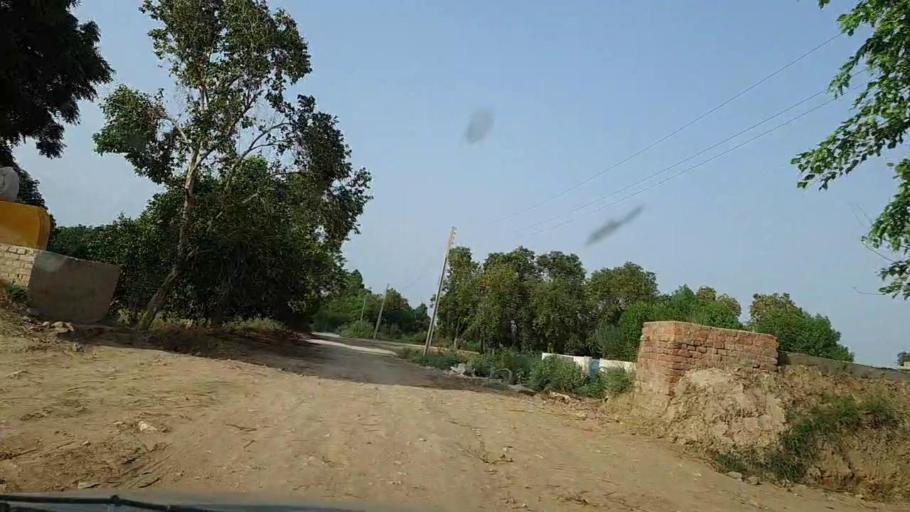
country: PK
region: Sindh
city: Kotri
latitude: 25.2376
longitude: 68.2638
